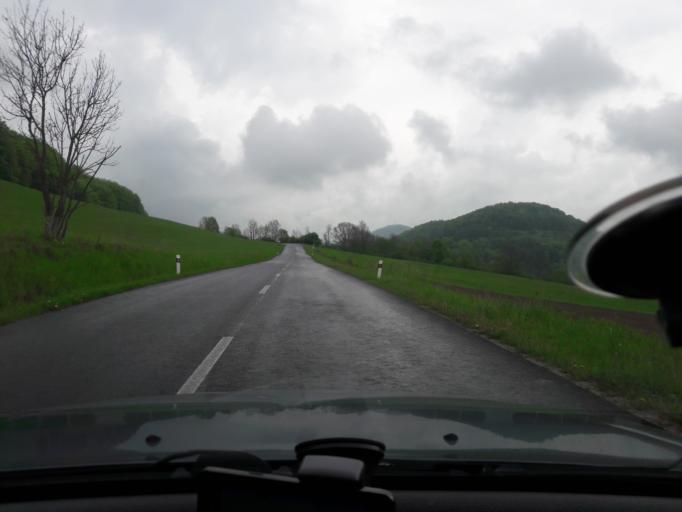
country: SK
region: Banskobystricky
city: Revuca
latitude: 48.7309
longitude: 20.0302
